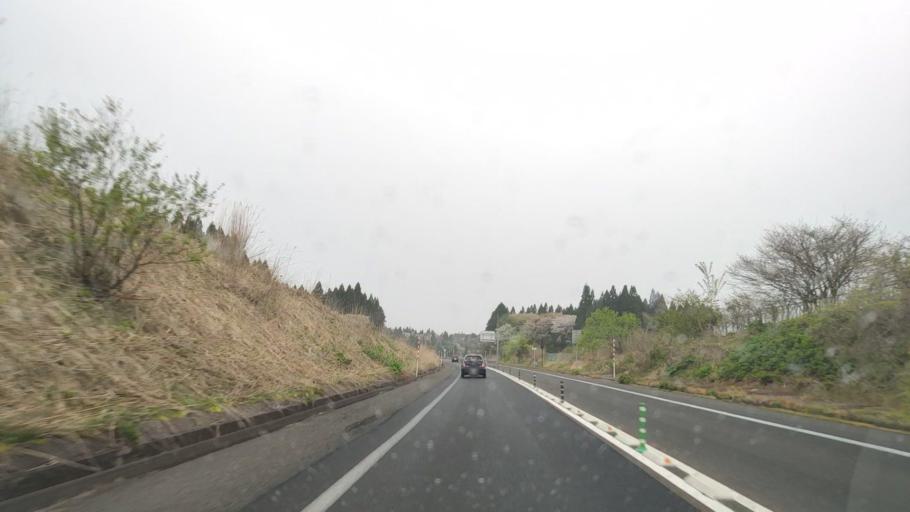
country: JP
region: Akita
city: Noshiromachi
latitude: 40.2083
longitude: 140.1889
